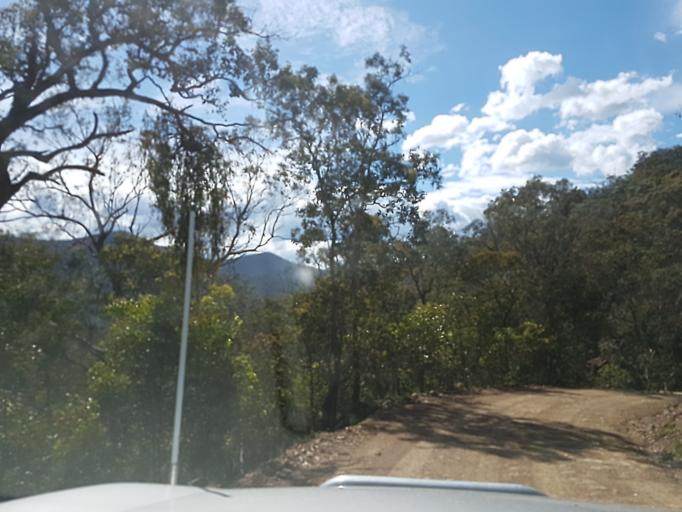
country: AU
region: Victoria
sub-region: Alpine
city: Mount Beauty
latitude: -37.3748
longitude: 147.0427
